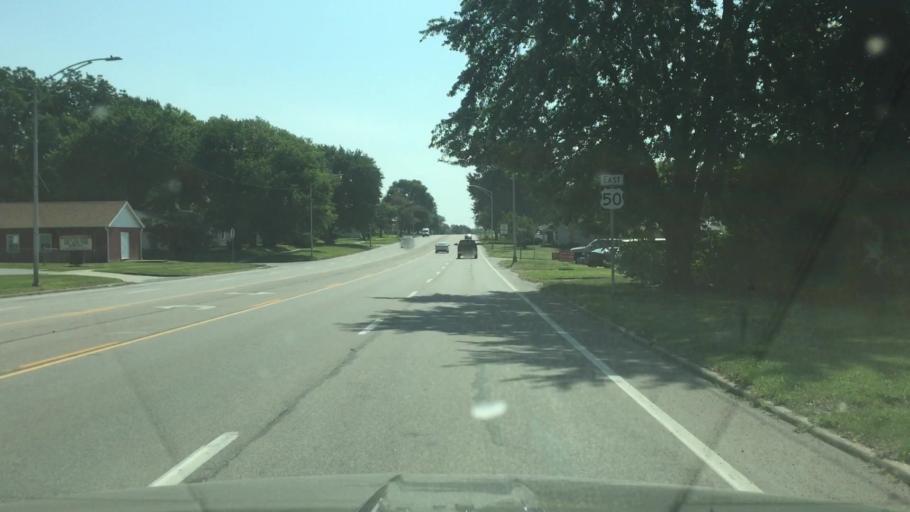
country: US
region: Missouri
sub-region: Pettis County
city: Sedalia
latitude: 38.7032
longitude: -93.2014
